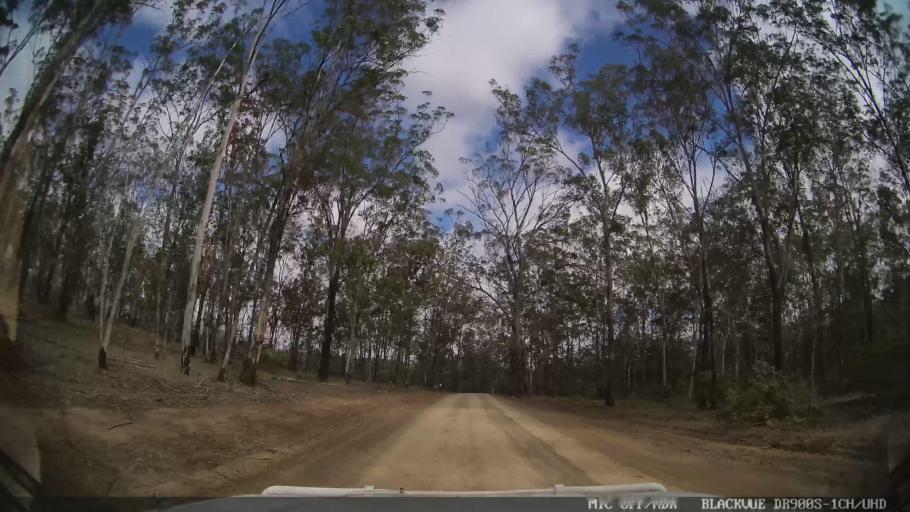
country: AU
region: Queensland
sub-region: Gladstone
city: Toolooa
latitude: -24.6825
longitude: 151.3321
